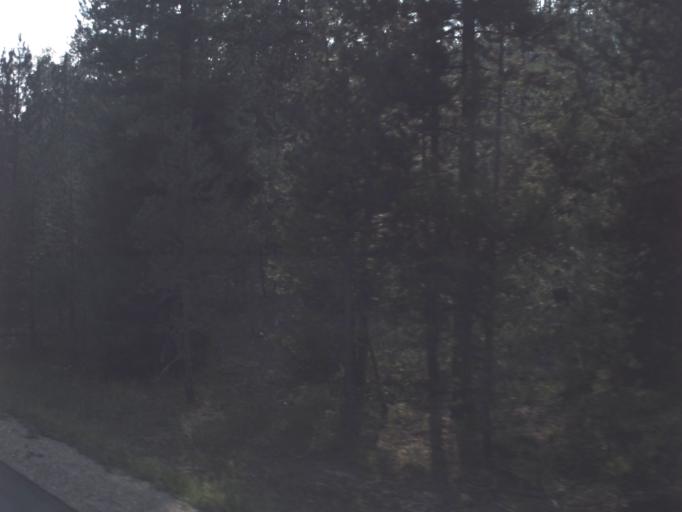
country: US
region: Utah
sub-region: Summit County
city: Francis
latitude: 40.5877
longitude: -111.0181
